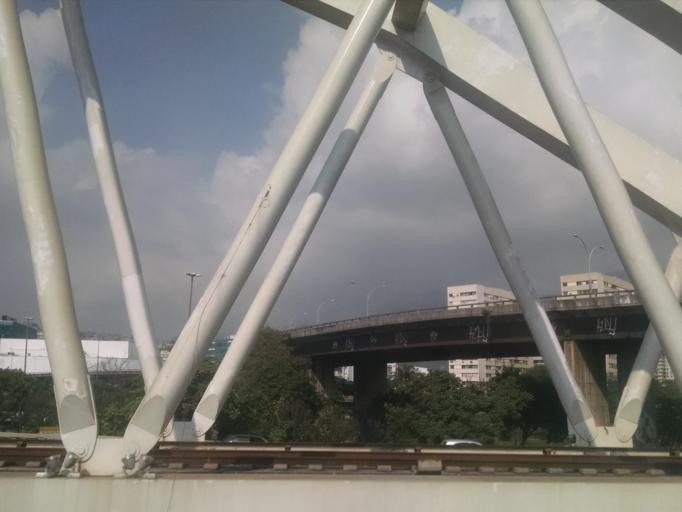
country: BR
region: Rio de Janeiro
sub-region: Rio De Janeiro
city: Rio de Janeiro
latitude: -22.9097
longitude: -43.2101
